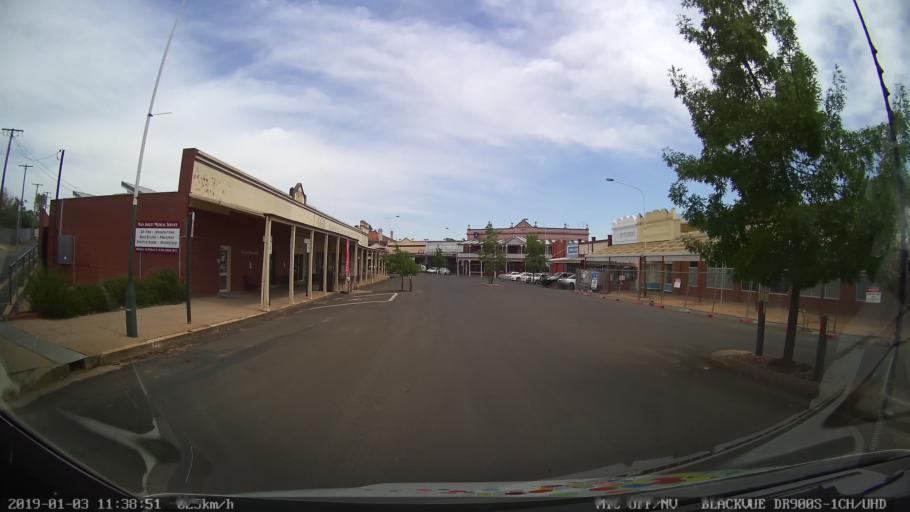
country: AU
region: New South Wales
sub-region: Weddin
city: Grenfell
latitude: -33.8945
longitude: 148.1626
